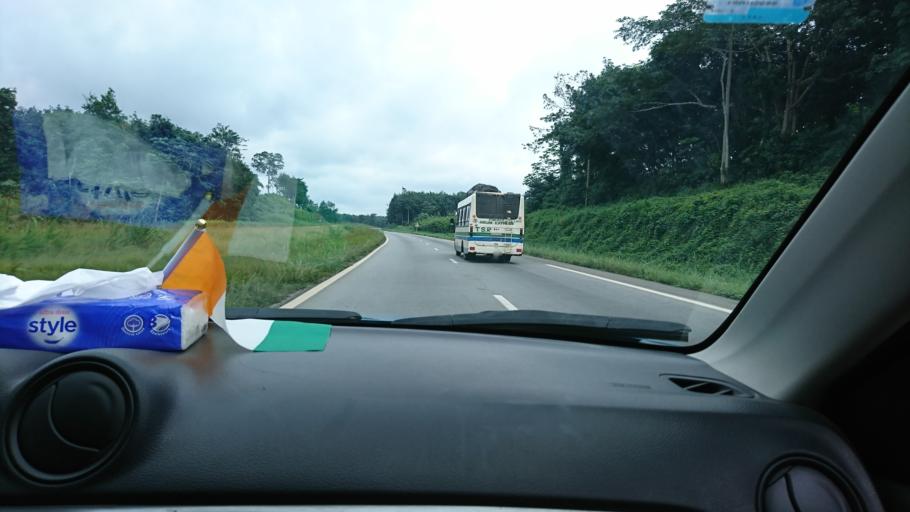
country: CI
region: Lagunes
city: Songon
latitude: 5.5375
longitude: -4.3027
